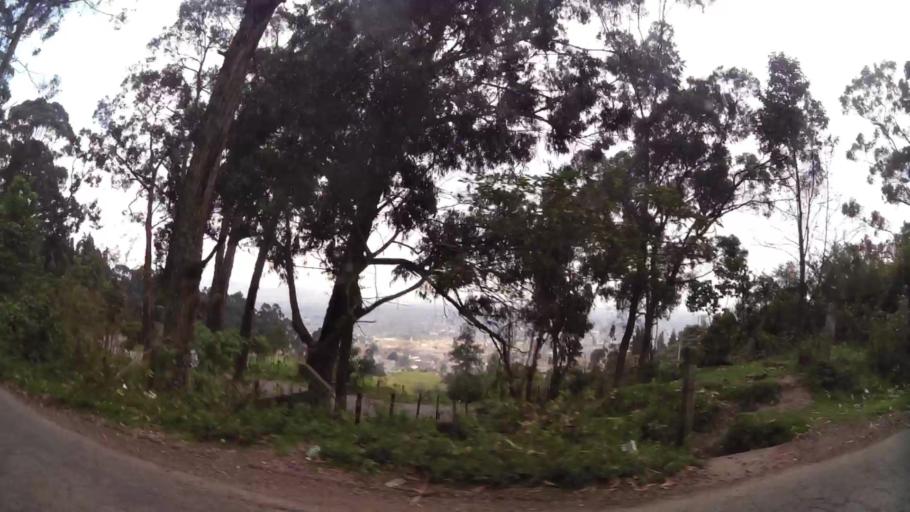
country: CO
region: Bogota D.C.
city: Bogota
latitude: 4.5951
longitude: -74.0640
